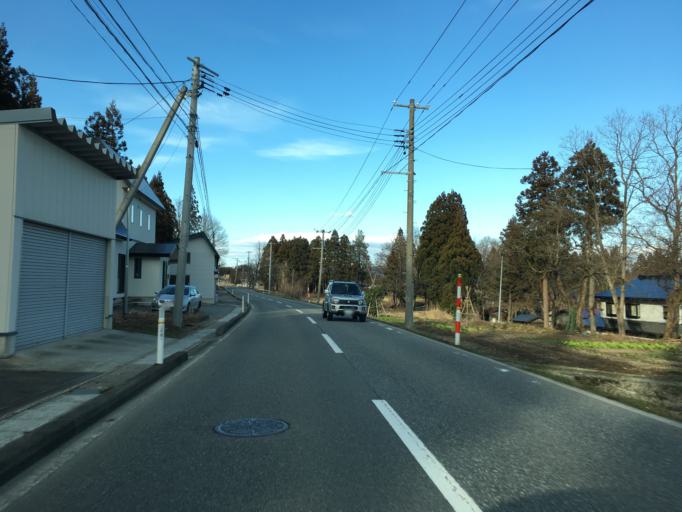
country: JP
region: Yamagata
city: Nagai
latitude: 38.0296
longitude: 139.9806
